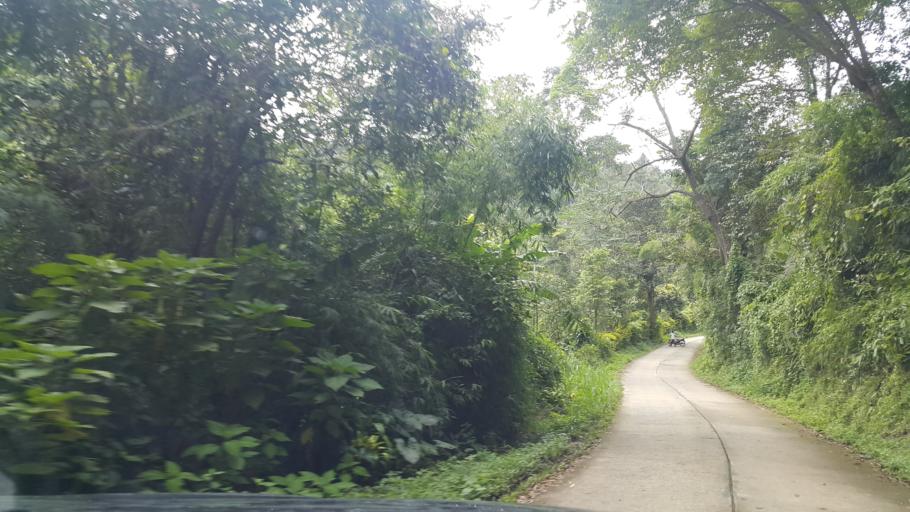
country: TH
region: Lampang
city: Wang Nuea
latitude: 19.0846
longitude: 99.3776
